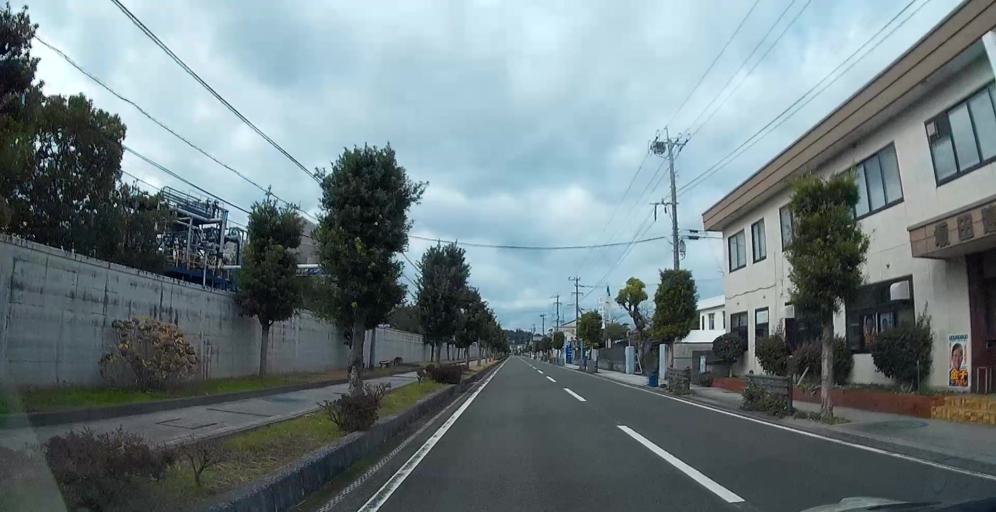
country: JP
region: Kumamoto
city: Minamata
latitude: 32.2109
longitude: 130.3943
